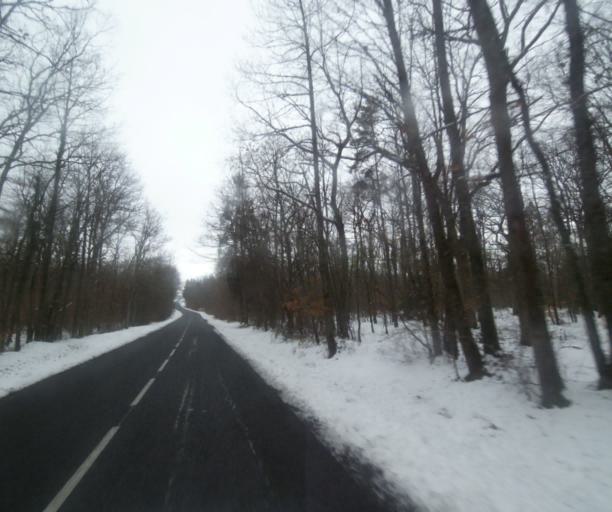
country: FR
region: Champagne-Ardenne
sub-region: Departement de la Haute-Marne
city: Laneuville-a-Remy
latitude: 48.4430
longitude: 4.8593
